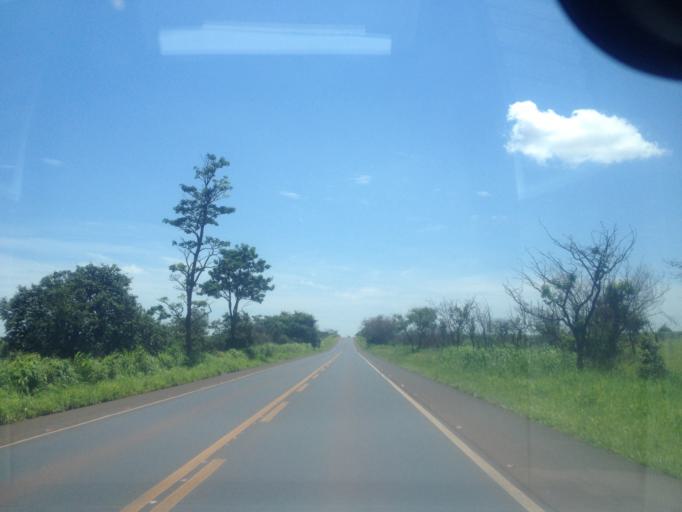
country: BR
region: Minas Gerais
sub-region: Ituiutaba
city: Ituiutaba
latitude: -18.8932
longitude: -49.2414
